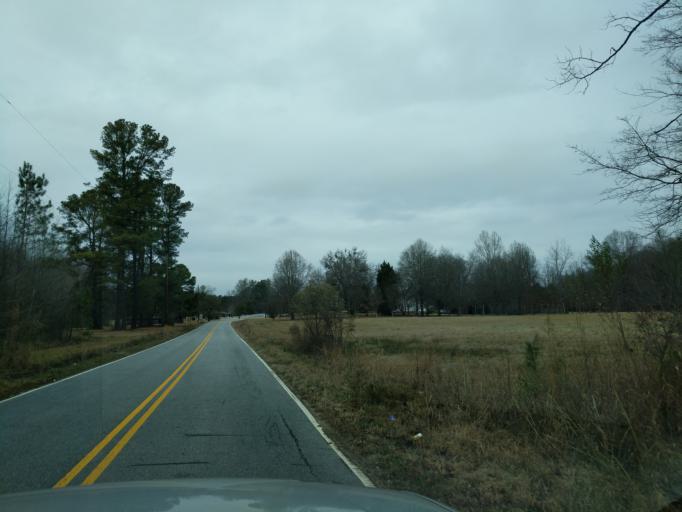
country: US
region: South Carolina
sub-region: Spartanburg County
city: Duncan
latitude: 34.8698
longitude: -82.1282
